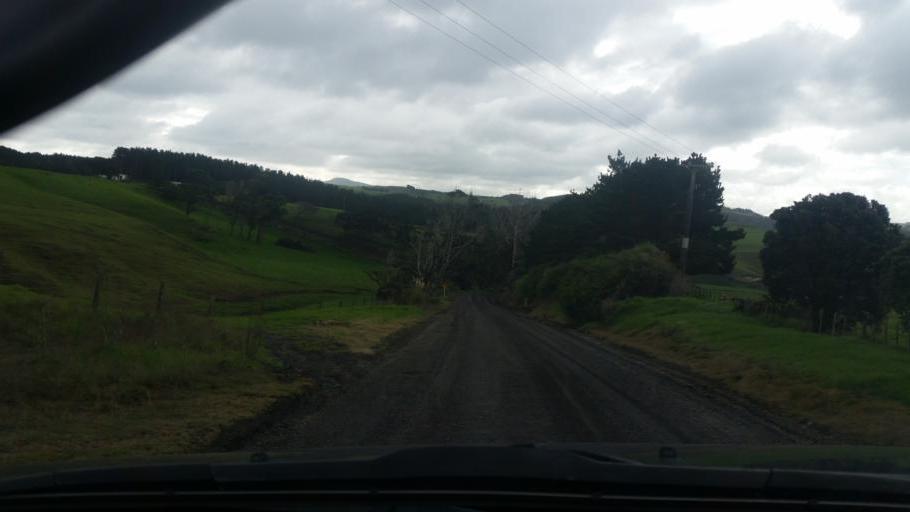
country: NZ
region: Northland
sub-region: Kaipara District
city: Dargaville
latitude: -35.8397
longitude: 173.6622
